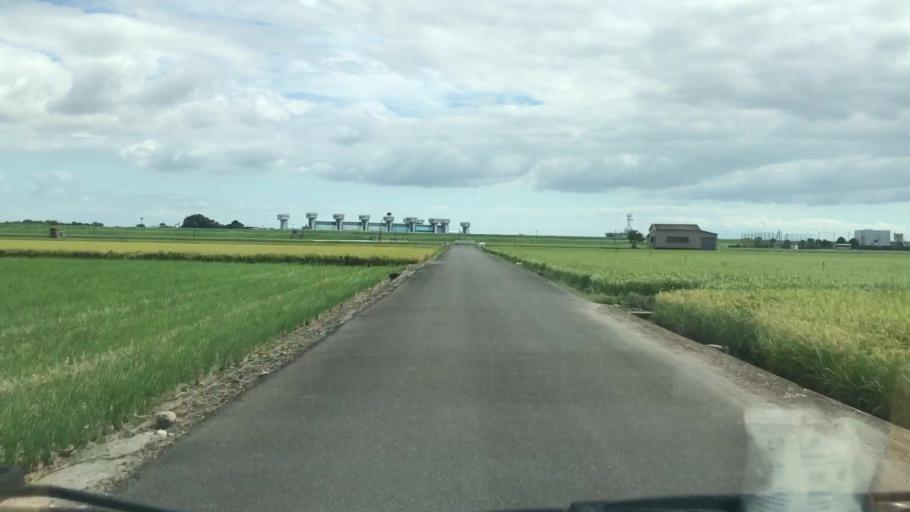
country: JP
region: Saga Prefecture
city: Saga-shi
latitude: 33.2103
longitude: 130.1851
